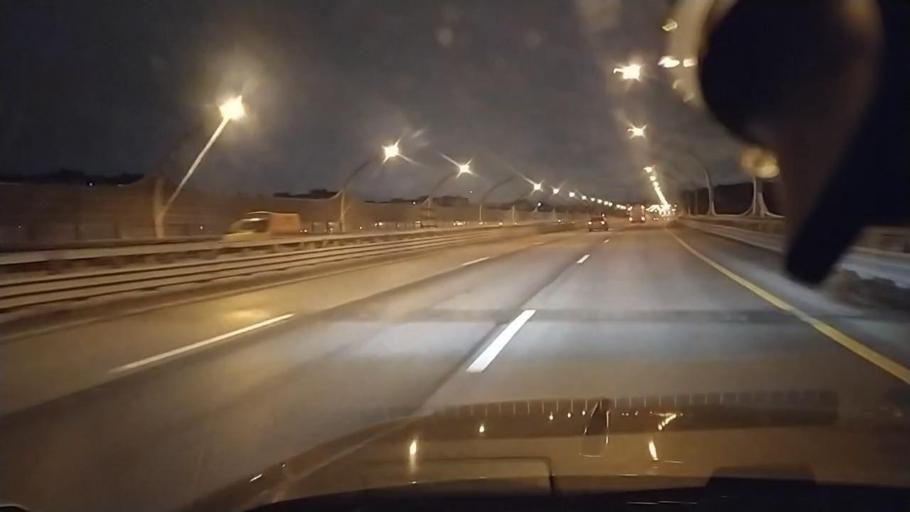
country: RU
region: Leningrad
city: Untolovo
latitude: 60.0209
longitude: 30.2196
